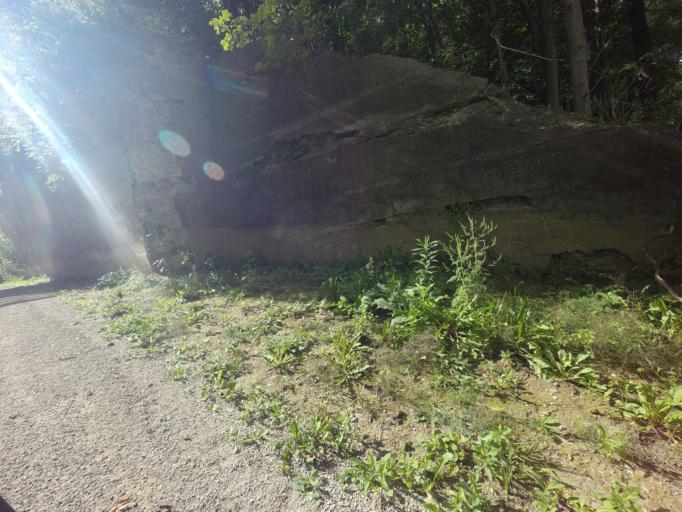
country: CA
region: Ontario
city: Huron East
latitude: 43.7347
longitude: -81.4201
